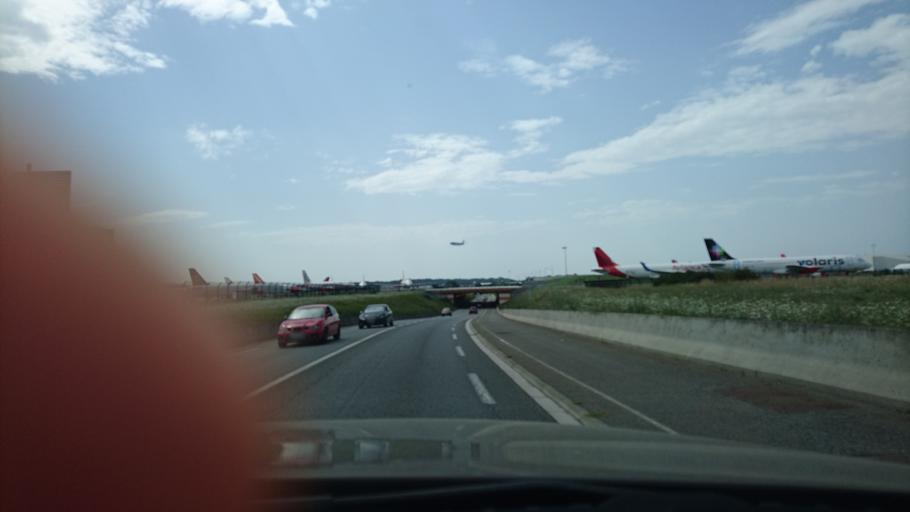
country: FR
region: Midi-Pyrenees
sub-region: Departement de la Haute-Garonne
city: Beauzelle
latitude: 43.6445
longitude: 1.3604
